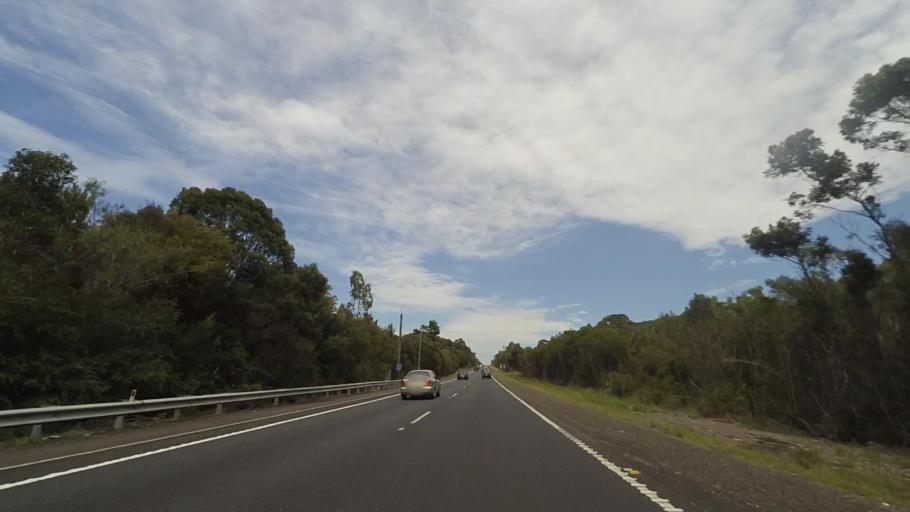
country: AU
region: New South Wales
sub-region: Wollongong
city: Helensburgh
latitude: -34.2172
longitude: 150.9561
